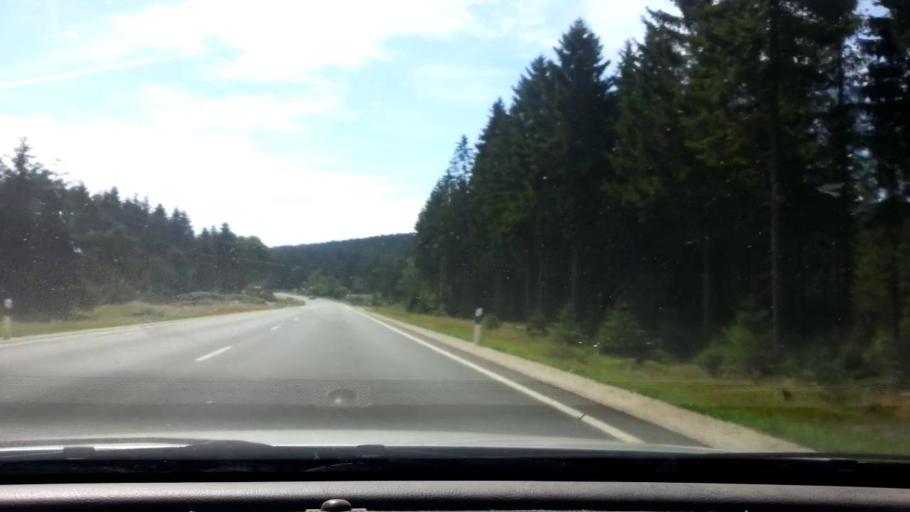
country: DE
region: Bavaria
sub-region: Upper Franconia
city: Fichtelberg
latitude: 50.0318
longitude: 11.8494
